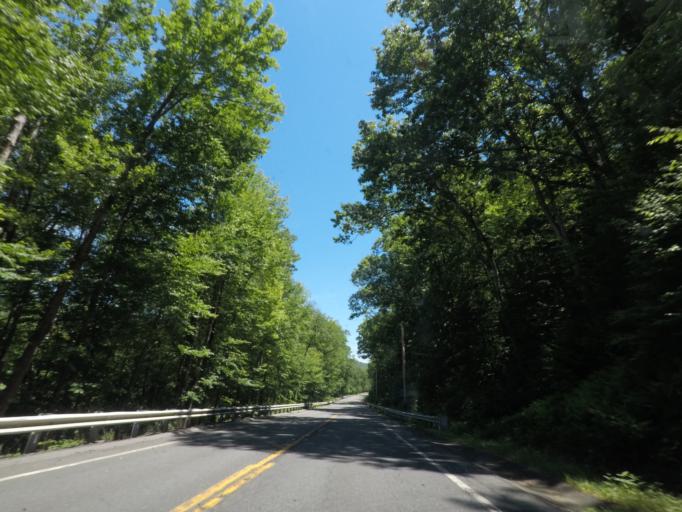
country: US
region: Massachusetts
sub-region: Hampshire County
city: Westhampton
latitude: 42.2481
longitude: -72.9273
